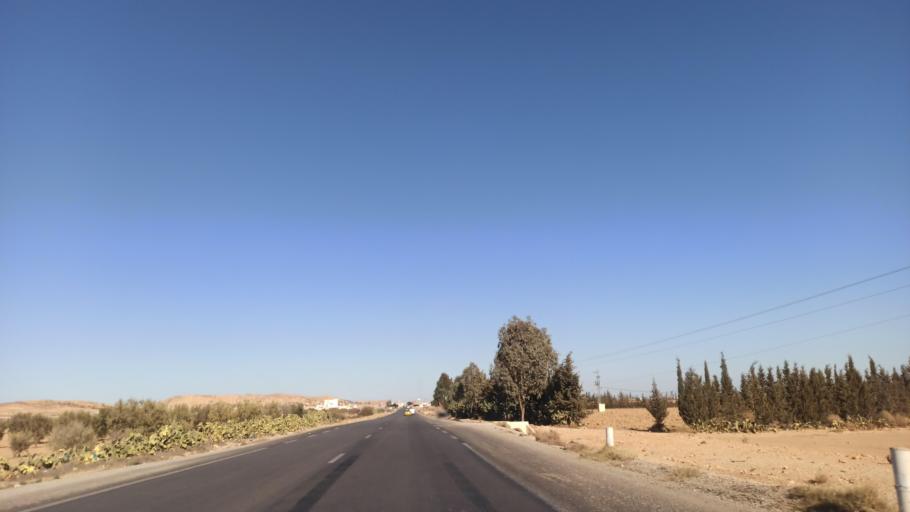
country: TN
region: Sidi Bu Zayd
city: Bi'r al Hufayy
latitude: 34.9070
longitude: 9.1791
